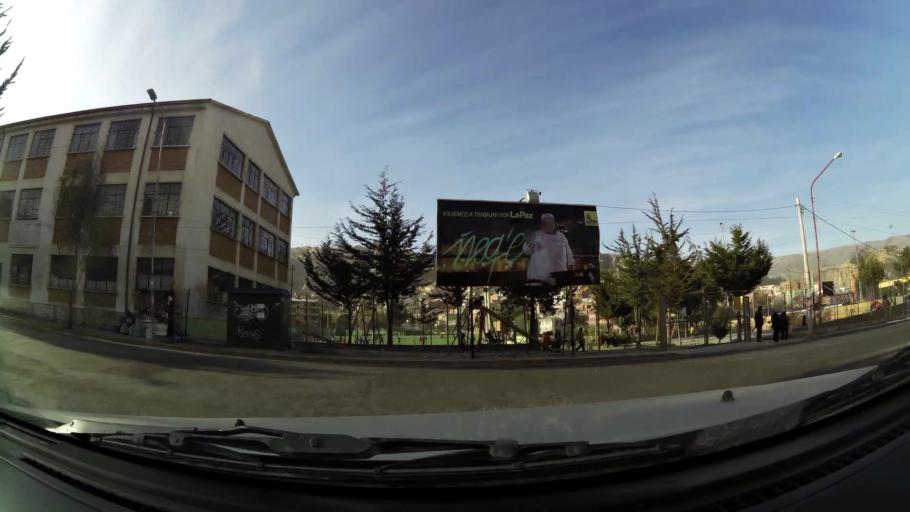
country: BO
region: La Paz
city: La Paz
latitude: -16.5239
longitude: -68.1050
